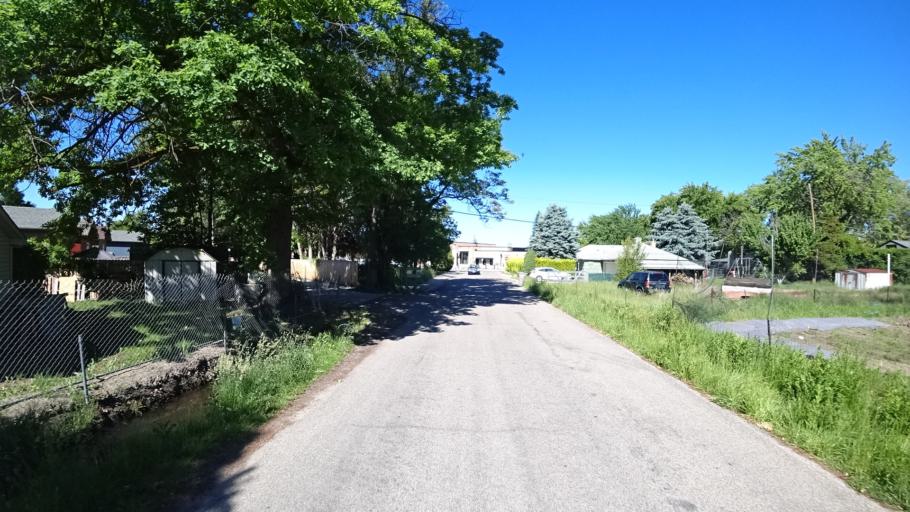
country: US
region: Idaho
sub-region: Ada County
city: Garden City
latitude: 43.6483
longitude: -116.2440
